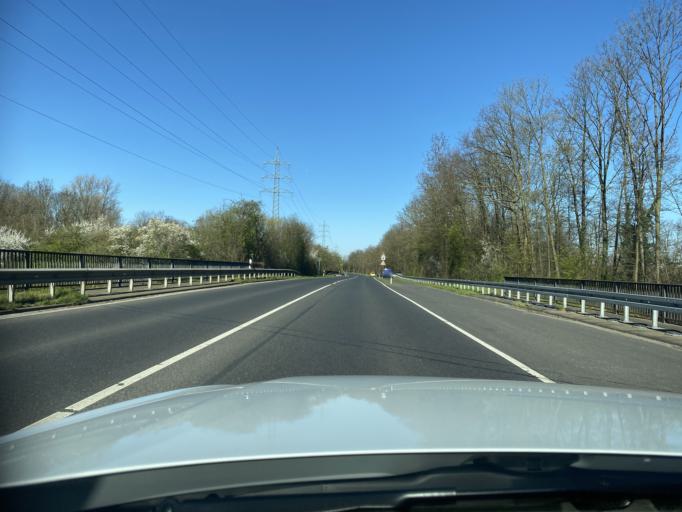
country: DE
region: North Rhine-Westphalia
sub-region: Regierungsbezirk Dusseldorf
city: Grevenbroich
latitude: 51.0977
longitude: 6.6062
